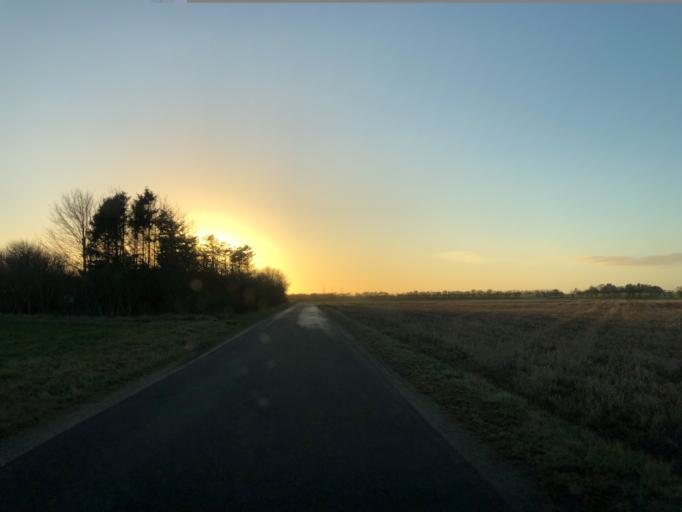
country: DK
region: Central Jutland
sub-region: Skive Kommune
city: Skive
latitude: 56.5347
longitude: 8.9283
